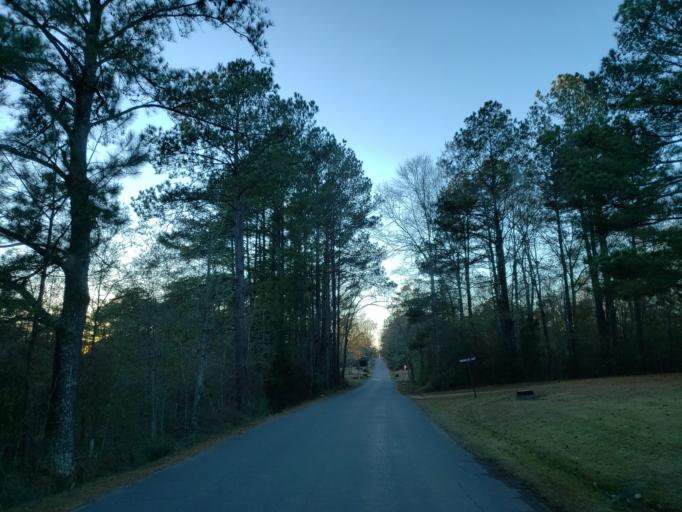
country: US
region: Mississippi
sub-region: Covington County
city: Collins
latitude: 31.5637
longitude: -89.4881
